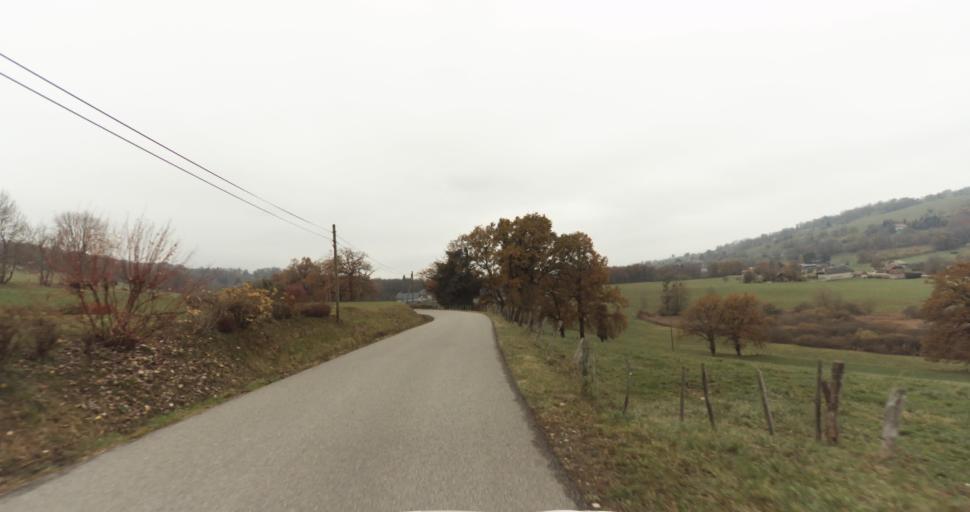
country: FR
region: Rhone-Alpes
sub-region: Departement de la Haute-Savoie
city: Cusy
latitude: 45.7594
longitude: 6.0206
